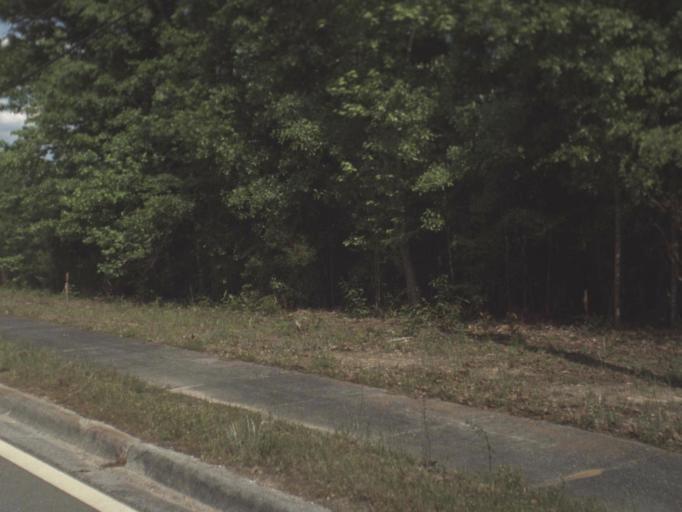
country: US
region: Florida
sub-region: Escambia County
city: Century
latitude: 30.9638
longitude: -87.2719
